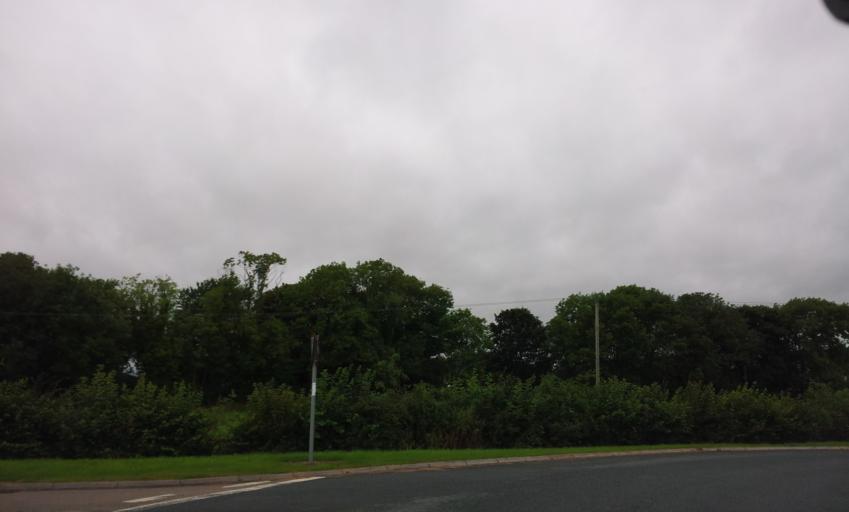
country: IE
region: Munster
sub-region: County Cork
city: Mitchelstown
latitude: 52.2849
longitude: -8.2179
